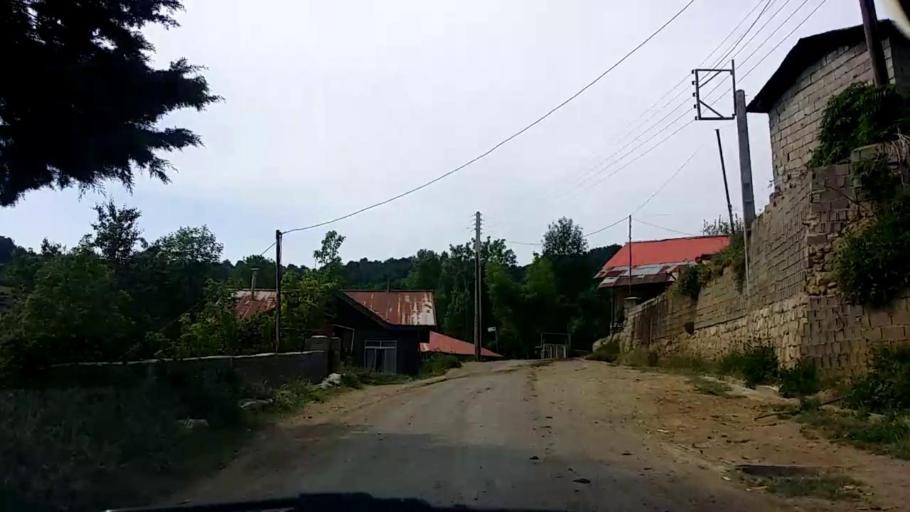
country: IR
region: Mazandaran
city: `Abbasabad
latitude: 36.5538
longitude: 51.1811
